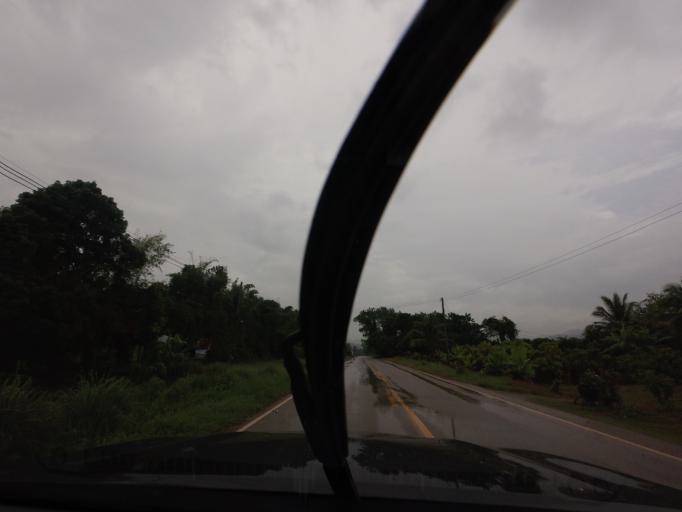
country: TH
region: Nong Khai
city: Sangkhom
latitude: 18.2055
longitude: 102.0687
